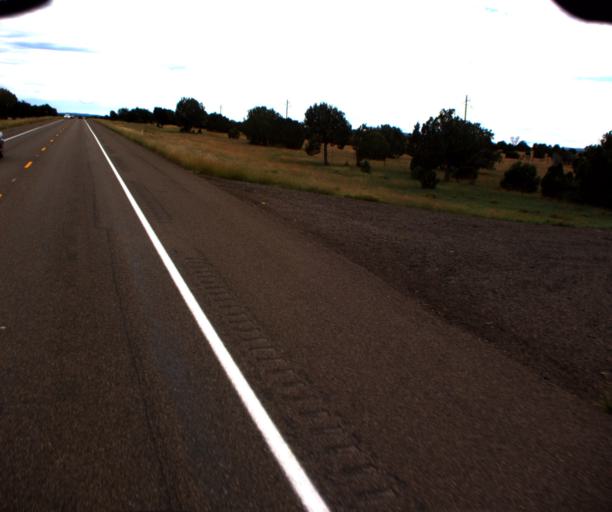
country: US
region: Arizona
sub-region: Navajo County
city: Show Low
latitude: 34.2980
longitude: -110.0341
